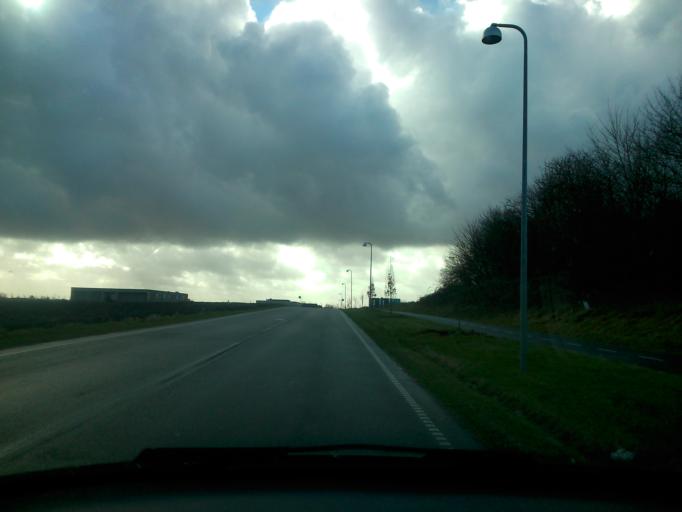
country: DK
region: Central Jutland
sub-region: Holstebro Kommune
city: Holstebro
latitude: 56.3948
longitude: 8.6120
